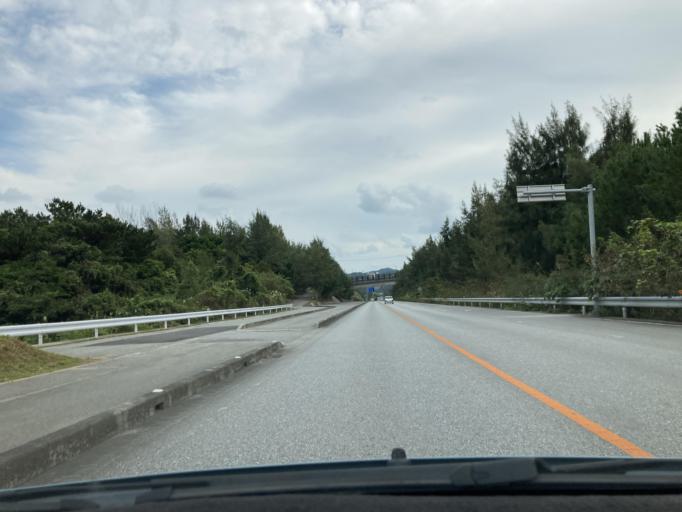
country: JP
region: Okinawa
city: Ishikawa
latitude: 26.5047
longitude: 127.8735
